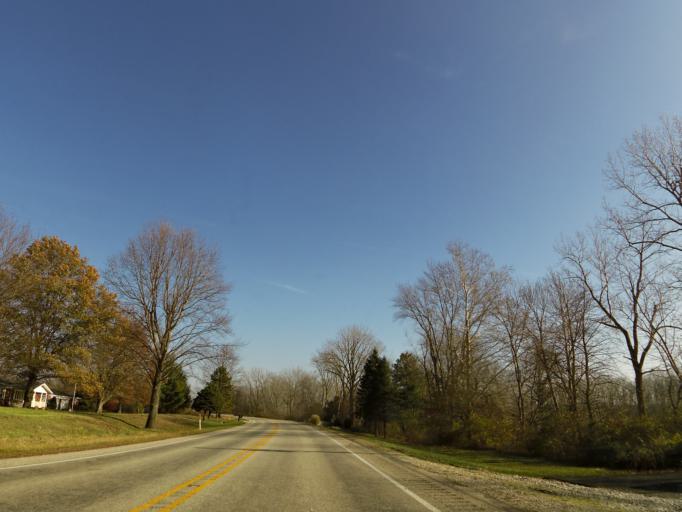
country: US
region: Indiana
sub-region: Rush County
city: Rushville
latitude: 39.6013
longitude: -85.4654
